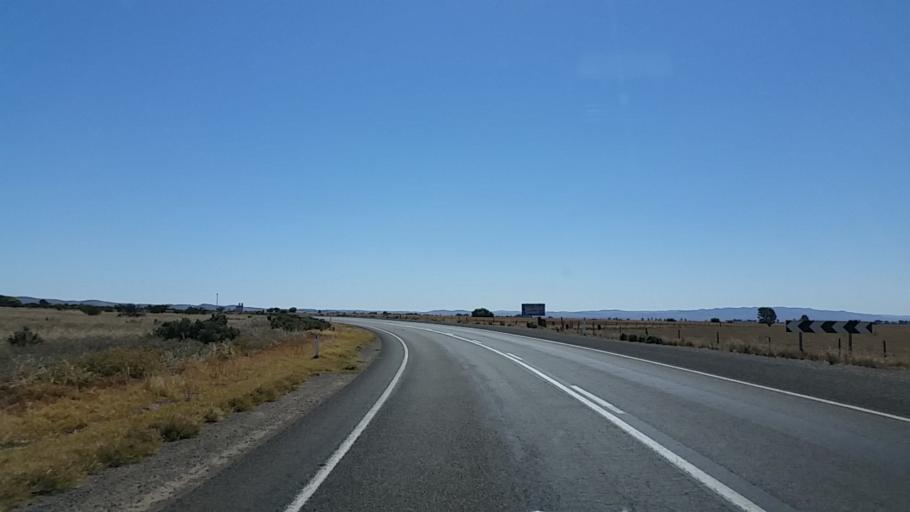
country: AU
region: South Australia
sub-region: Peterborough
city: Peterborough
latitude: -32.7463
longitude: 138.6362
